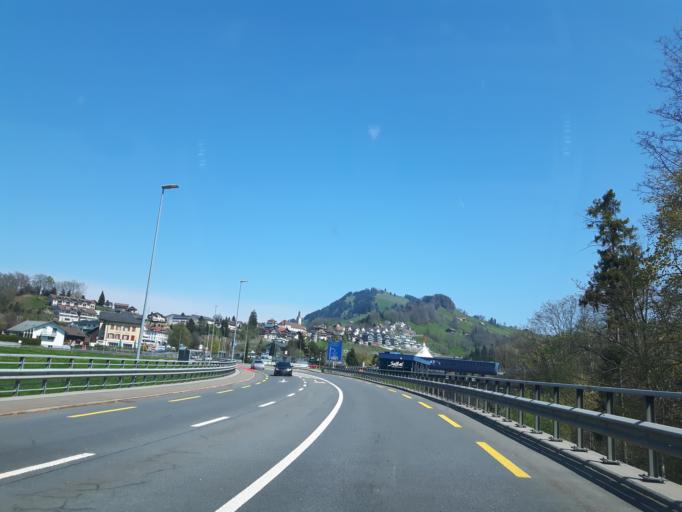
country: CH
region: Schwyz
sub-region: Bezirk Schwyz
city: Sattel
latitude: 47.0774
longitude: 8.6333
